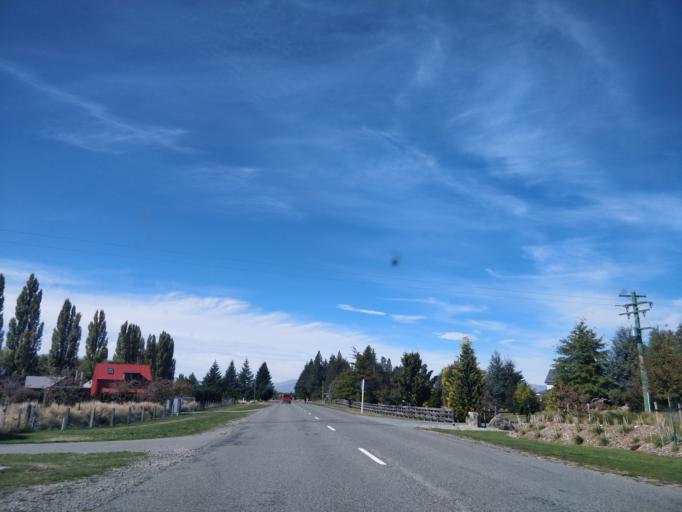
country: NZ
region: Otago
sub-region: Queenstown-Lakes District
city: Wanaka
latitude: -44.2432
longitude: 170.0888
